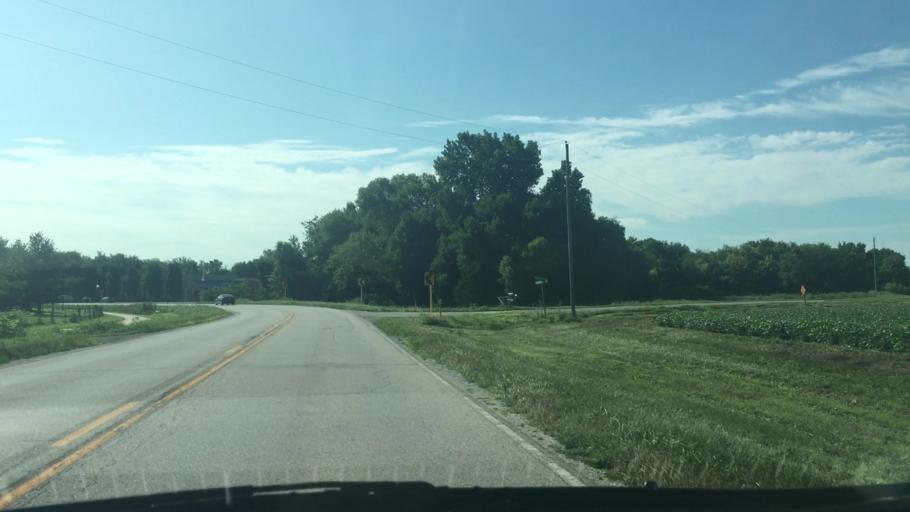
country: US
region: Iowa
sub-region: Johnson County
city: North Liberty
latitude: 41.7346
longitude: -91.5808
